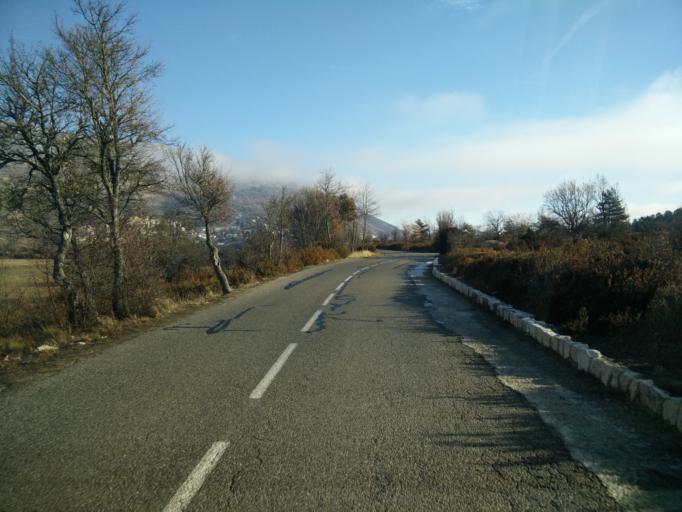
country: FR
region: Provence-Alpes-Cote d'Azur
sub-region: Departement des Alpes-Maritimes
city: Tourrettes-sur-Loup
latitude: 43.7872
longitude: 7.0282
